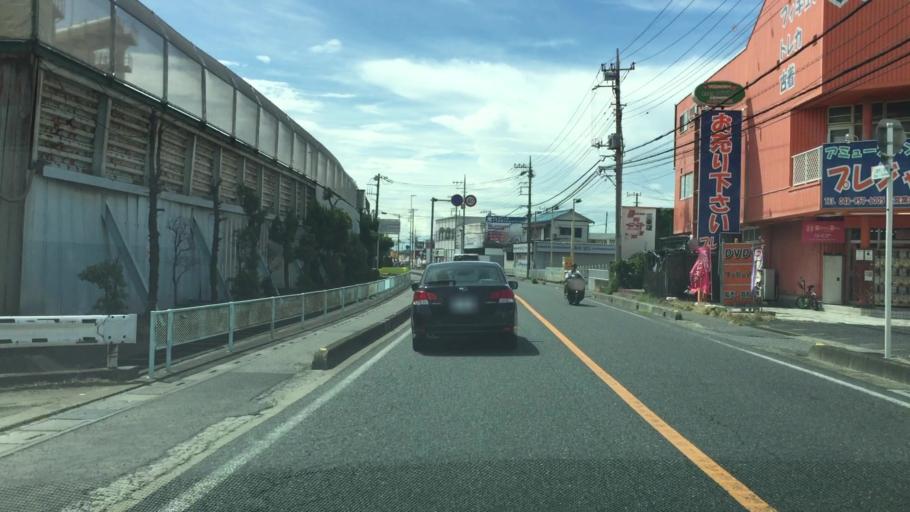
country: JP
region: Saitama
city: Yashio-shi
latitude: 35.8497
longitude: 139.8585
